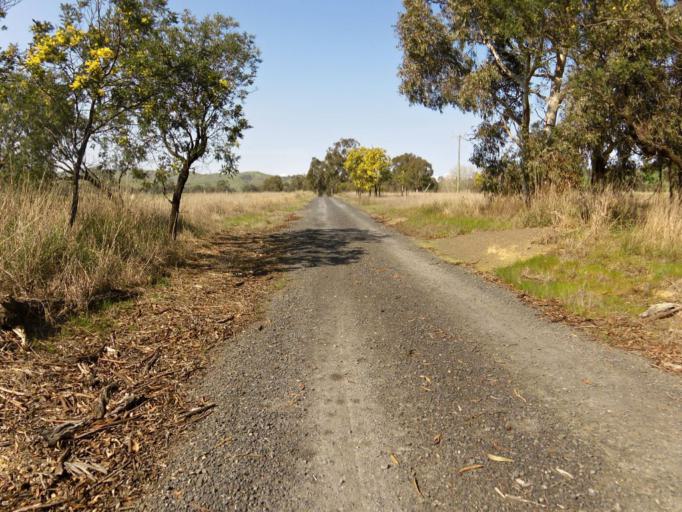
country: AU
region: Victoria
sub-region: Murrindindi
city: Alexandra
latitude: -37.0132
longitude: 145.7655
